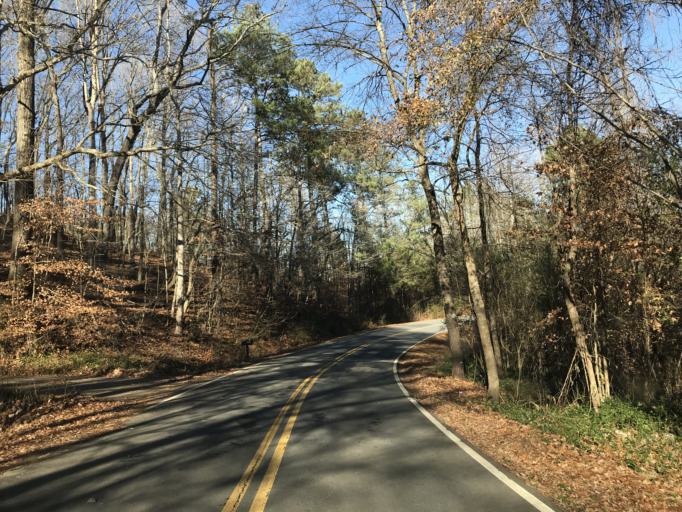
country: US
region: Georgia
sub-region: Paulding County
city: Dallas
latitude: 33.9939
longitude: -84.8931
